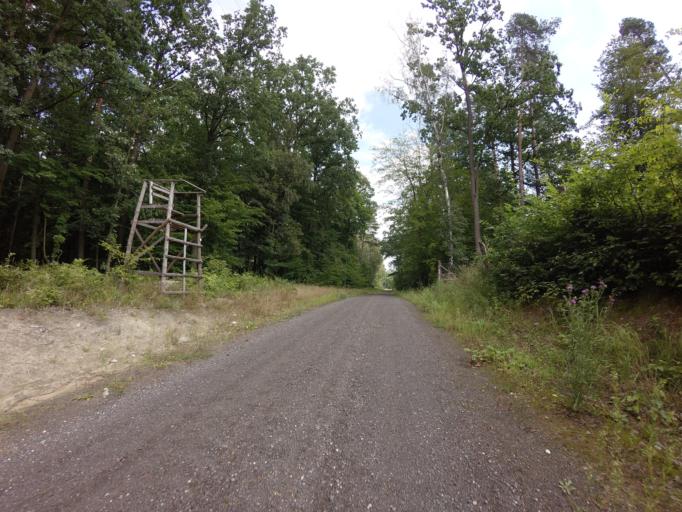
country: PL
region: Kujawsko-Pomorskie
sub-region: Powiat bydgoski
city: Koronowo
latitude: 53.3779
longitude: 17.9797
